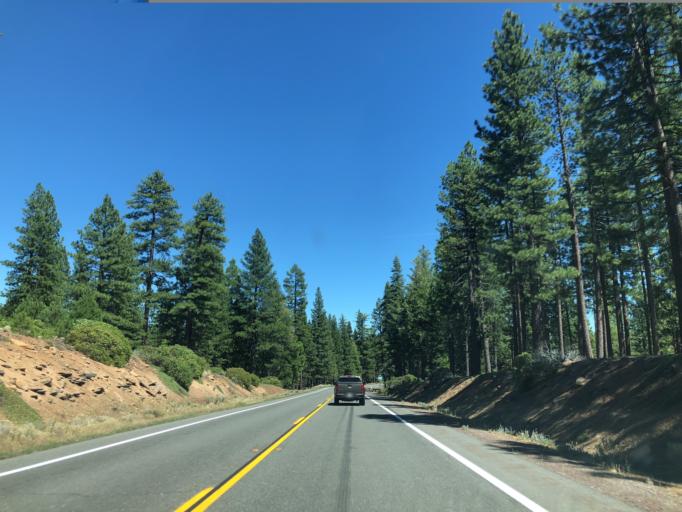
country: US
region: California
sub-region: Lassen County
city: Susanville
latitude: 40.4257
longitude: -120.7925
